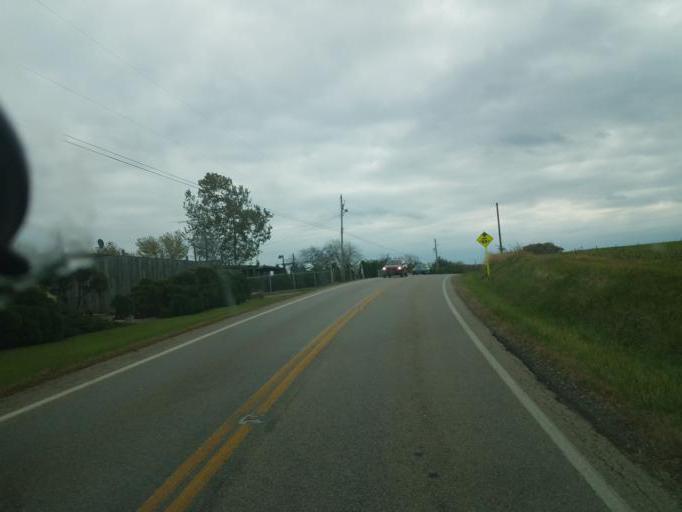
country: US
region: Ohio
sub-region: Ashland County
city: Loudonville
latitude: 40.6305
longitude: -82.2029
